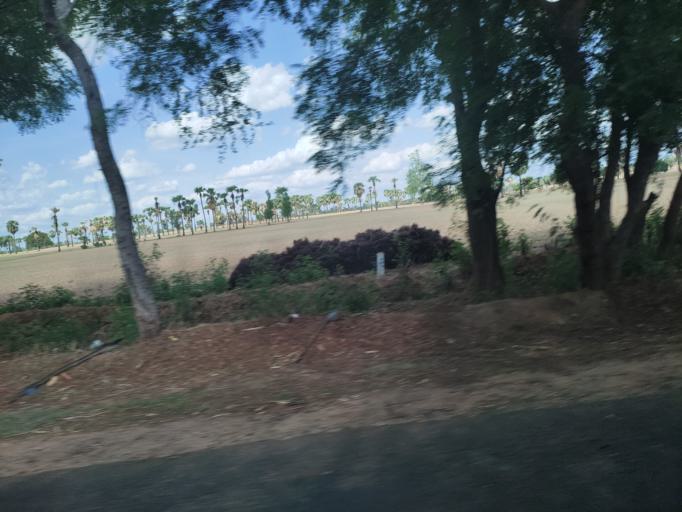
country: MM
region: Magway
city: Magway
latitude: 20.2175
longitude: 95.0178
